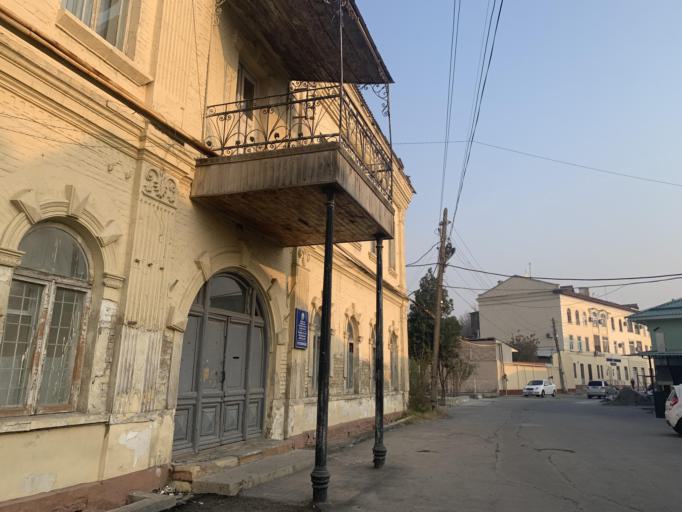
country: UZ
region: Fergana
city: Qo`qon
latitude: 40.5375
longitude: 70.9317
